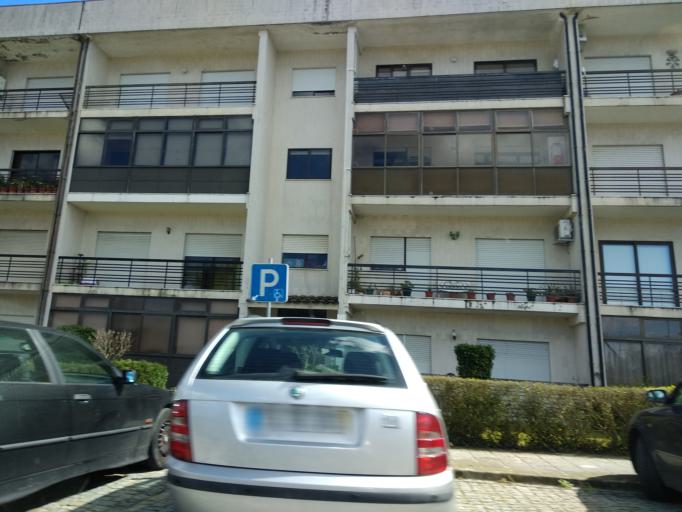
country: PT
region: Braga
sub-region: Braga
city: Braga
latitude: 41.5630
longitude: -8.4112
